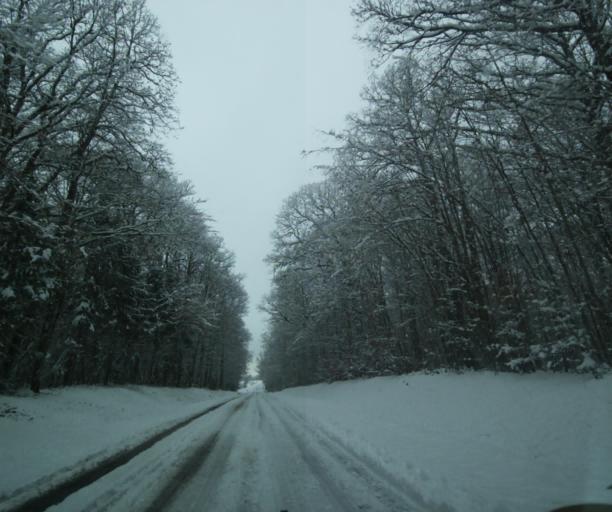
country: FR
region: Champagne-Ardenne
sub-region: Departement de la Haute-Marne
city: Montier-en-Der
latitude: 48.5417
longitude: 4.8053
